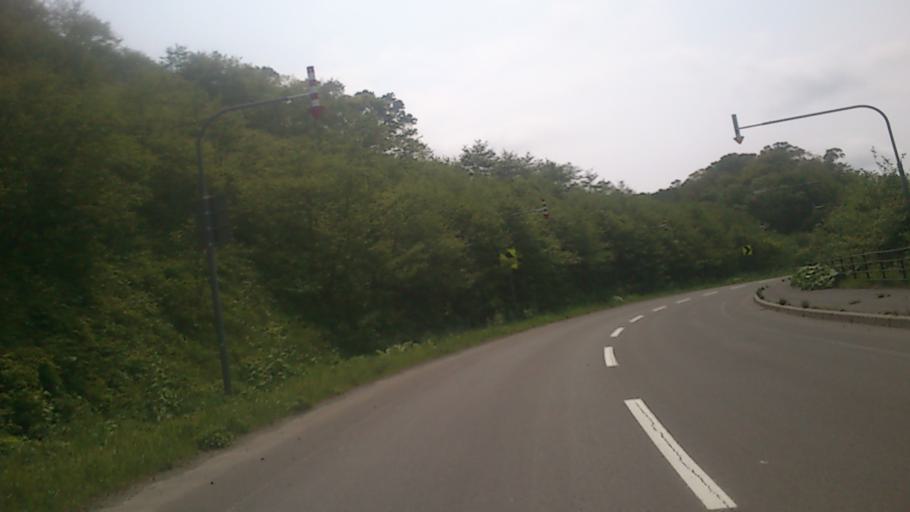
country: JP
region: Hokkaido
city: Nemuro
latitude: 43.2781
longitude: 145.5613
